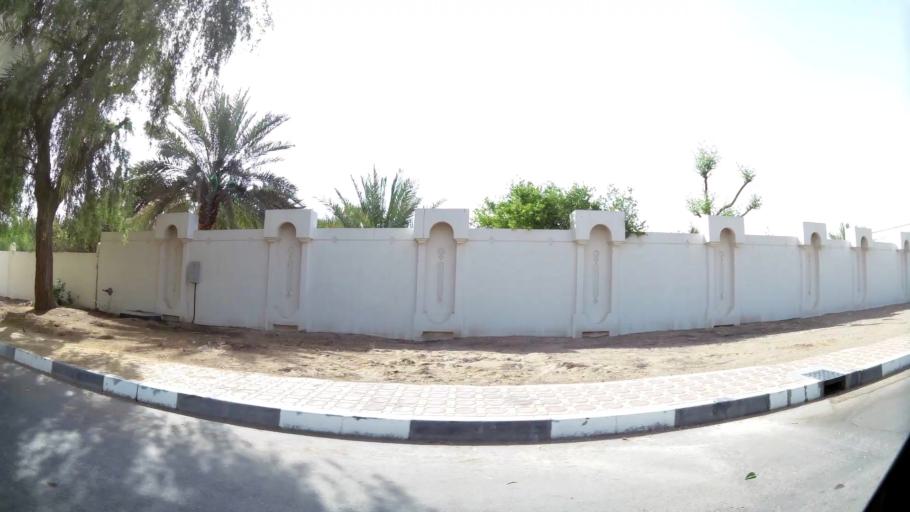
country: AE
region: Abu Dhabi
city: Al Ain
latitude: 24.2476
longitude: 55.6940
